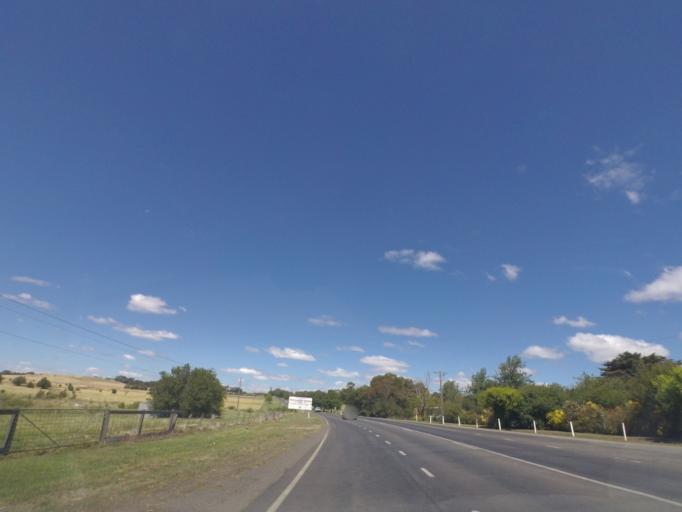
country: AU
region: Victoria
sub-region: Mount Alexander
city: Castlemaine
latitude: -37.2374
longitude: 144.4206
